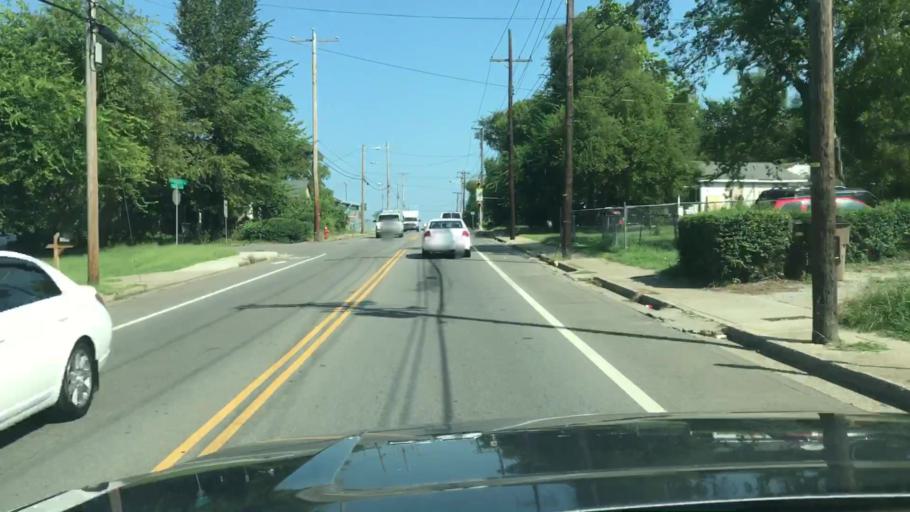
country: US
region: Tennessee
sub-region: Davidson County
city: Nashville
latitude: 36.1739
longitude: -86.8085
